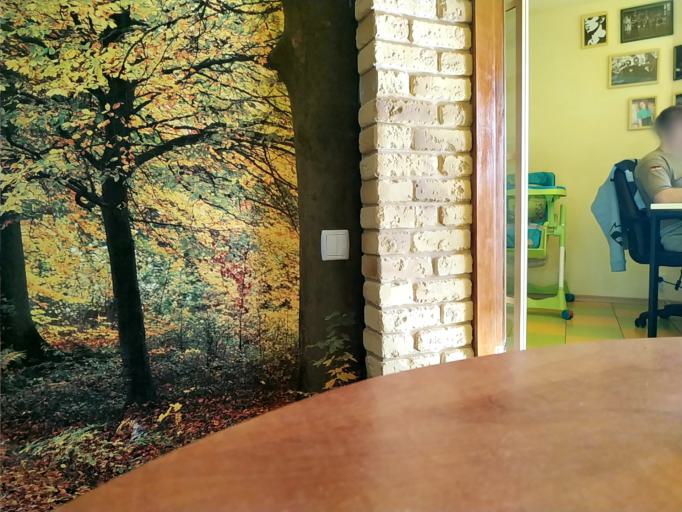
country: RU
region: Tverskaya
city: Vasil'yevskiy Mokh
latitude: 57.1789
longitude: 35.7816
